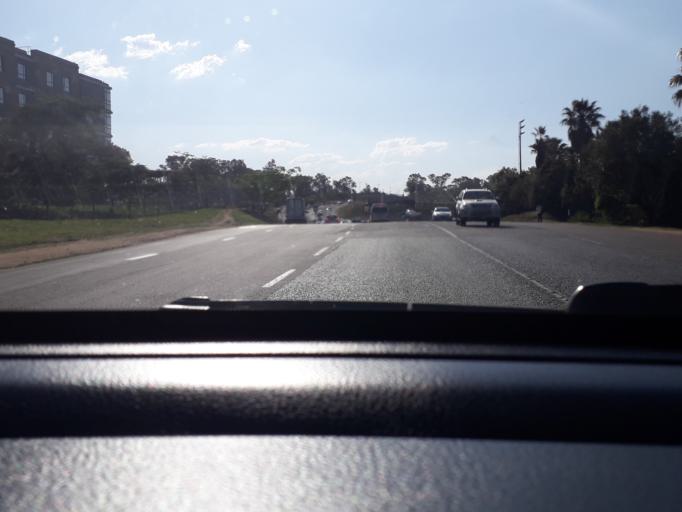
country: ZA
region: Gauteng
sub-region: City of Johannesburg Metropolitan Municipality
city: Midrand
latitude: -26.0433
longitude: 28.0925
